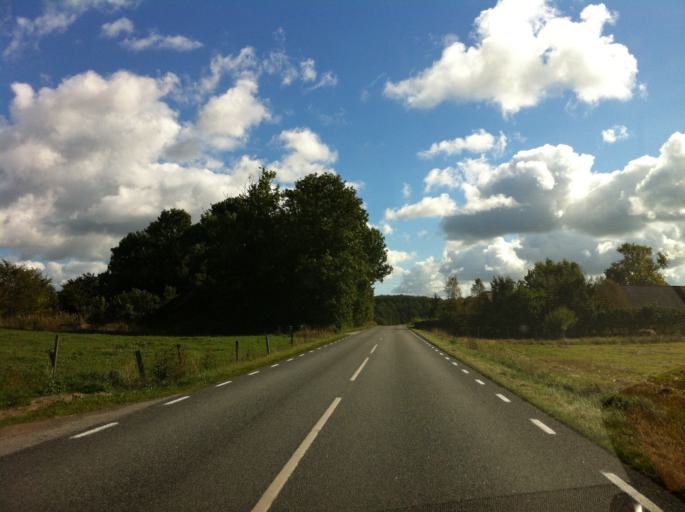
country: SE
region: Skane
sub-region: Kristianstads Kommun
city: Degeberga
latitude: 55.7859
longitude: 13.8703
